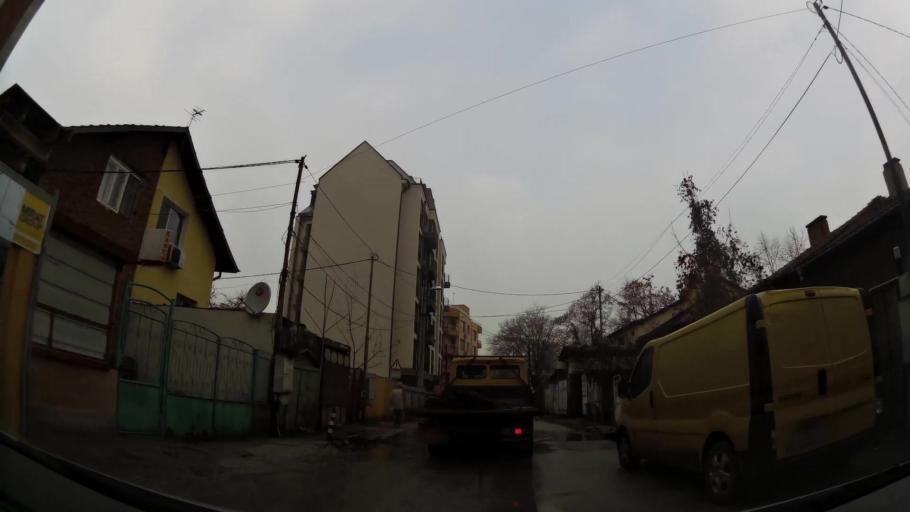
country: BG
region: Sofia-Capital
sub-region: Stolichna Obshtina
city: Sofia
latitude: 42.7307
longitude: 23.2999
